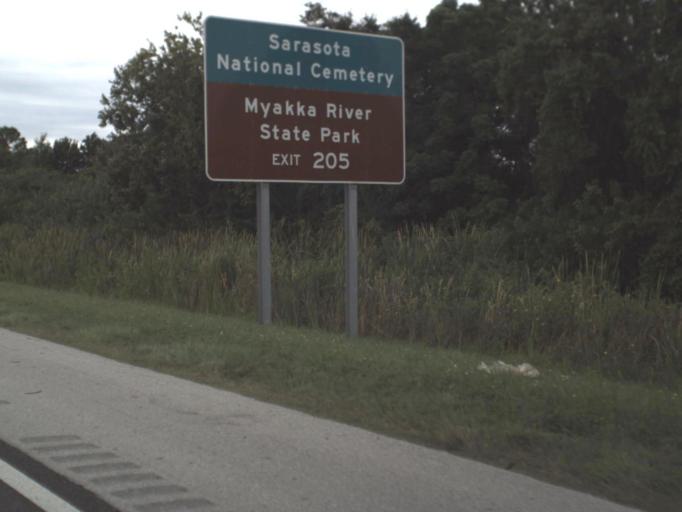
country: US
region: Florida
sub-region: Sarasota County
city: Lake Sarasota
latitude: 27.2831
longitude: -82.4490
